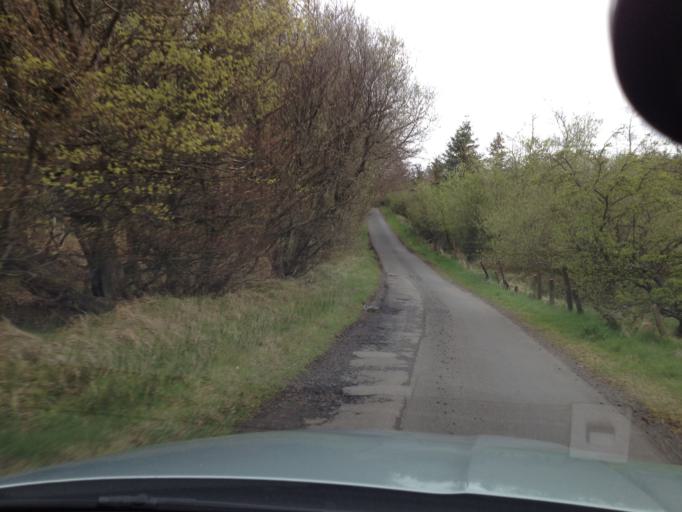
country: GB
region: Scotland
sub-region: West Lothian
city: Linlithgow
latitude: 55.9358
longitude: -3.6063
